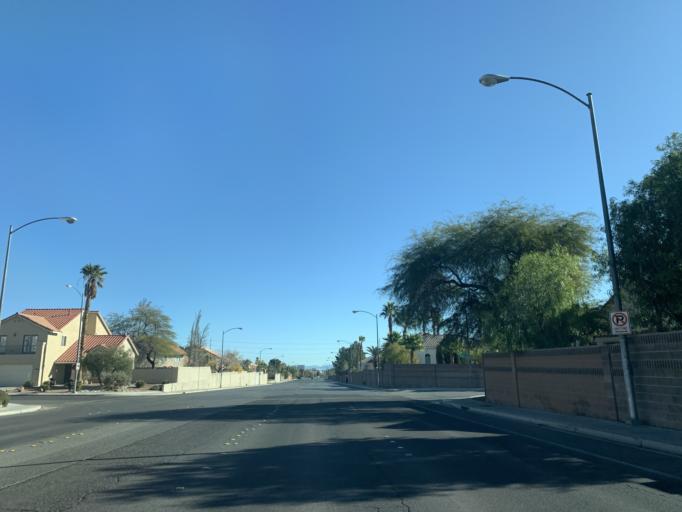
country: US
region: Nevada
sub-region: Clark County
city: Spring Valley
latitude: 36.1223
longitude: -115.2840
